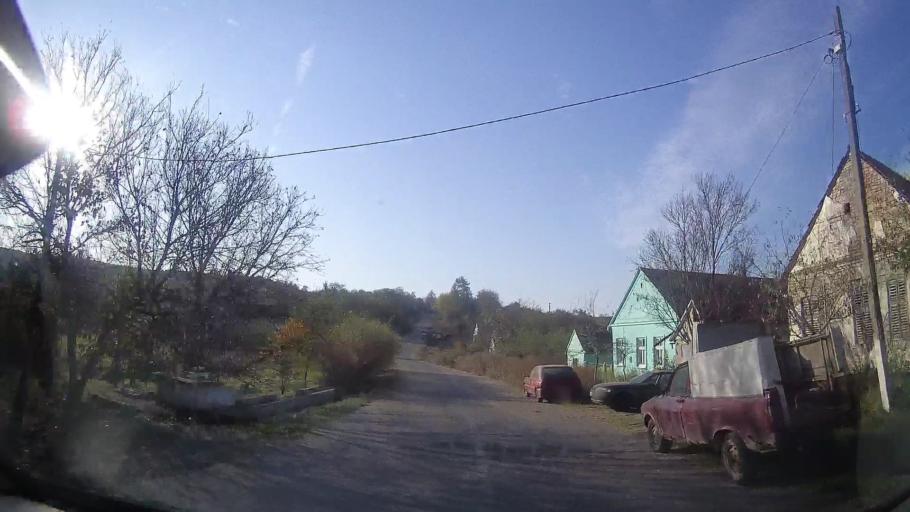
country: RO
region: Timis
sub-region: Comuna Bogda
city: Bogda
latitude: 45.9596
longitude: 21.6144
